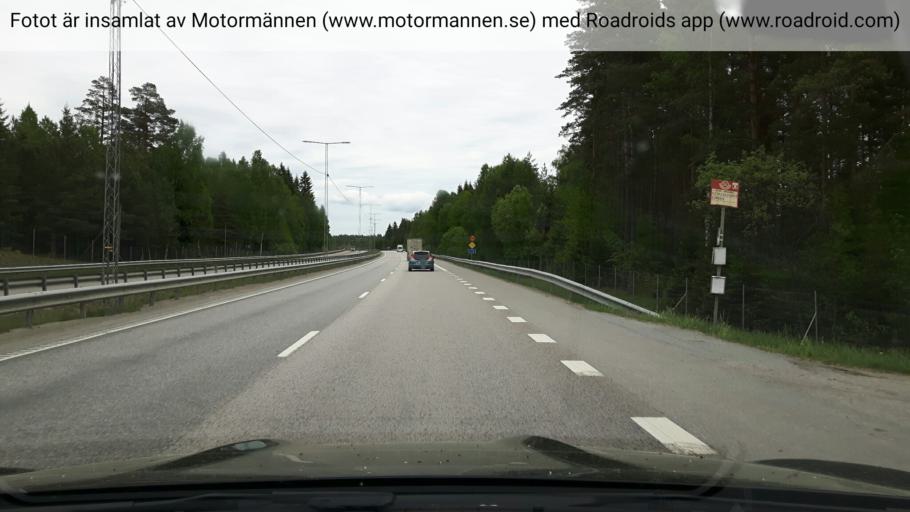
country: SE
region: Stockholm
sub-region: Osterakers Kommun
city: Akersberga
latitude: 59.4933
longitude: 18.1873
